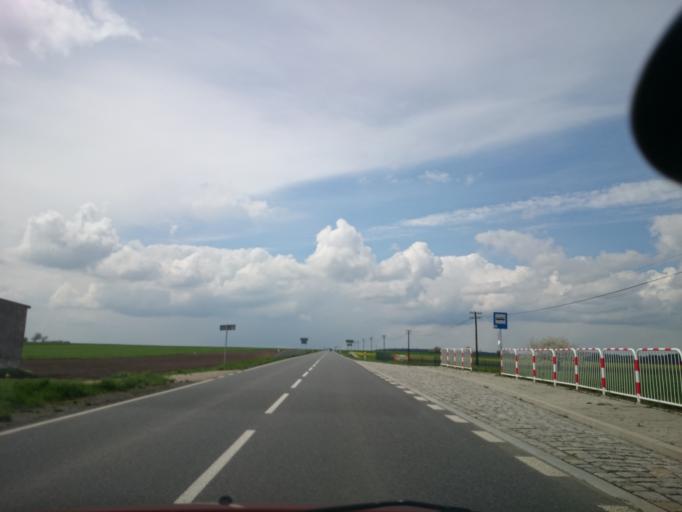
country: PL
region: Opole Voivodeship
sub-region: Powiat krapkowicki
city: Rozwadza
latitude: 50.4946
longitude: 18.1199
